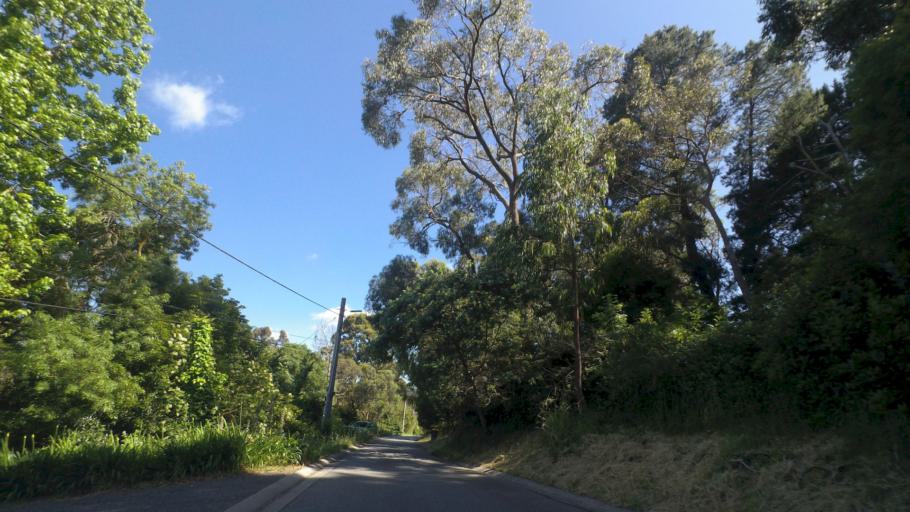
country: AU
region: Victoria
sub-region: Yarra Ranges
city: Mount Evelyn
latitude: -37.8005
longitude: 145.3786
